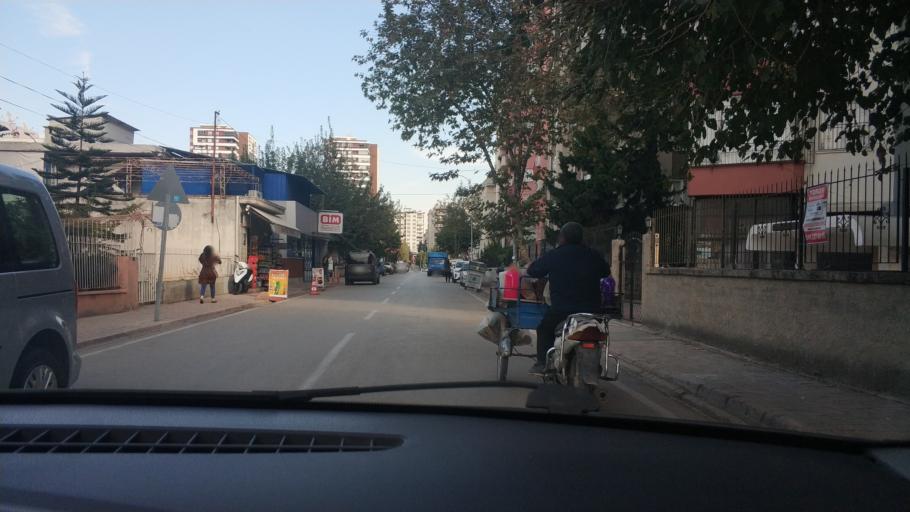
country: TR
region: Adana
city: Adana
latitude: 37.0065
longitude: 35.3186
